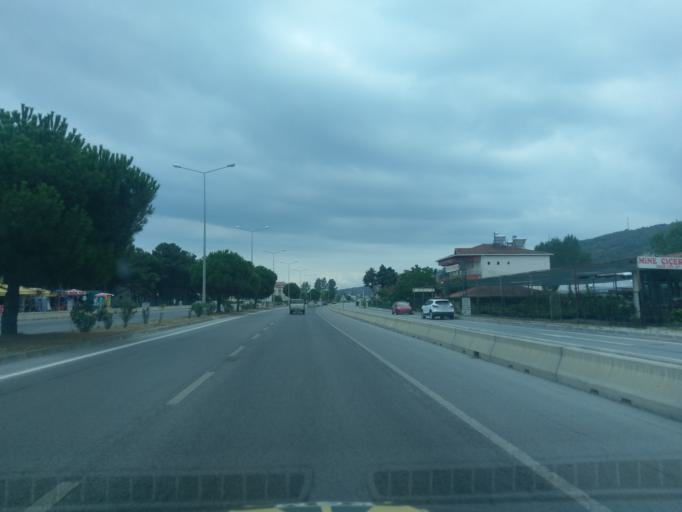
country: TR
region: Samsun
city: Taflan
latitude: 41.3965
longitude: 36.1969
